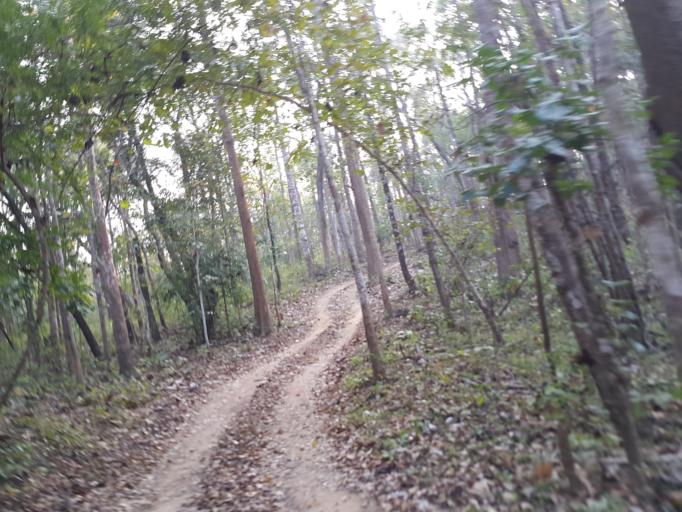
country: TH
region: Lamphun
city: Li
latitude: 17.6166
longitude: 98.8961
